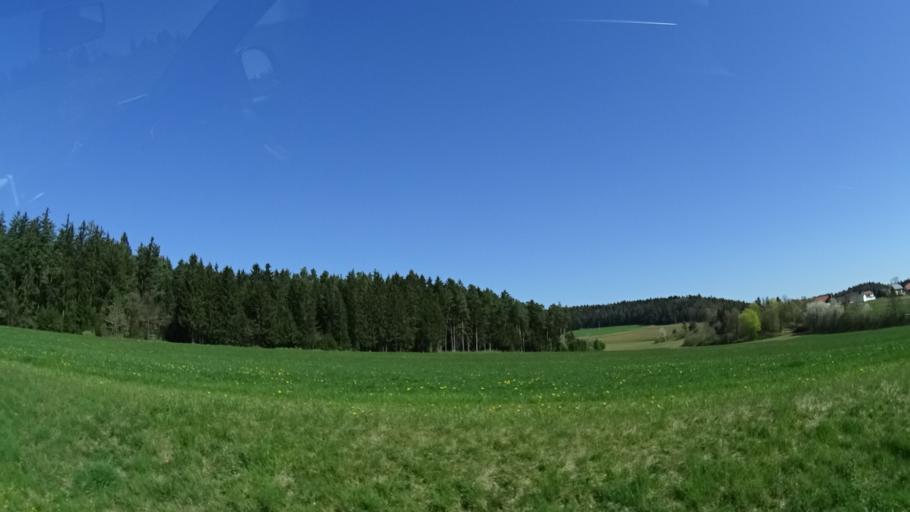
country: DE
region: Bavaria
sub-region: Upper Palatinate
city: Kastl
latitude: 49.3868
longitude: 11.7016
